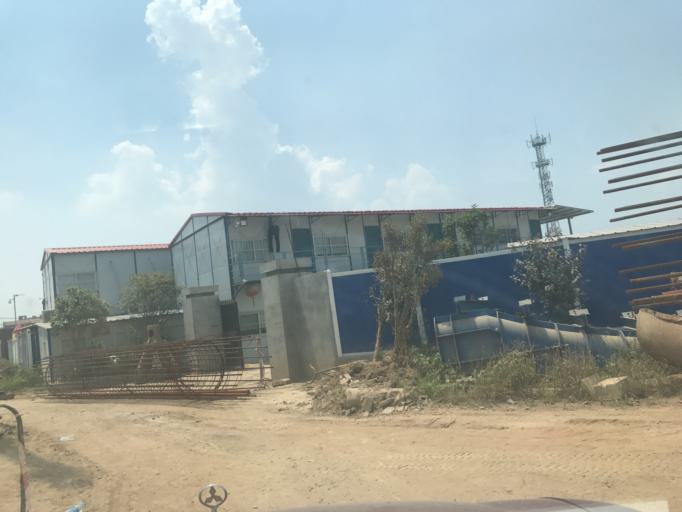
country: CN
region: Hubei
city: Zhanjiaji
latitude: 30.6905
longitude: 114.3395
